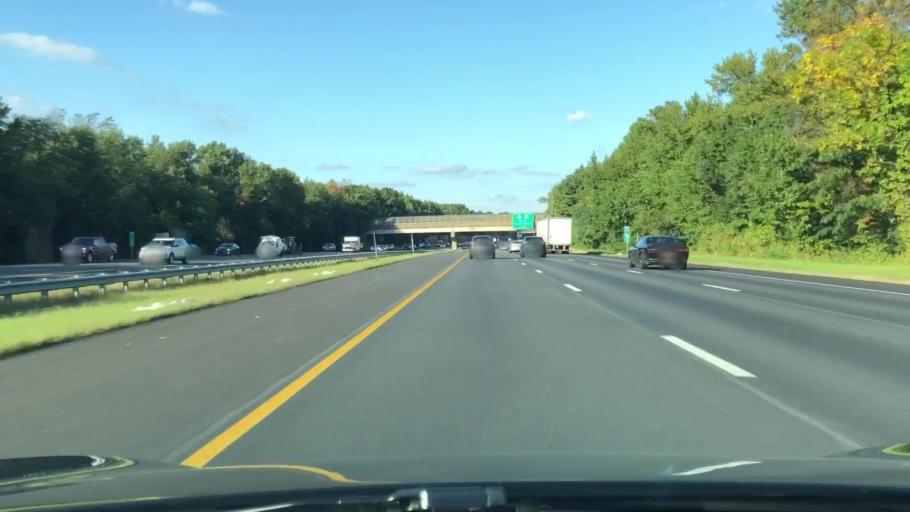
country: US
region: New Jersey
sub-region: Camden County
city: Kingston Estates
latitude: 39.9193
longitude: -74.9795
